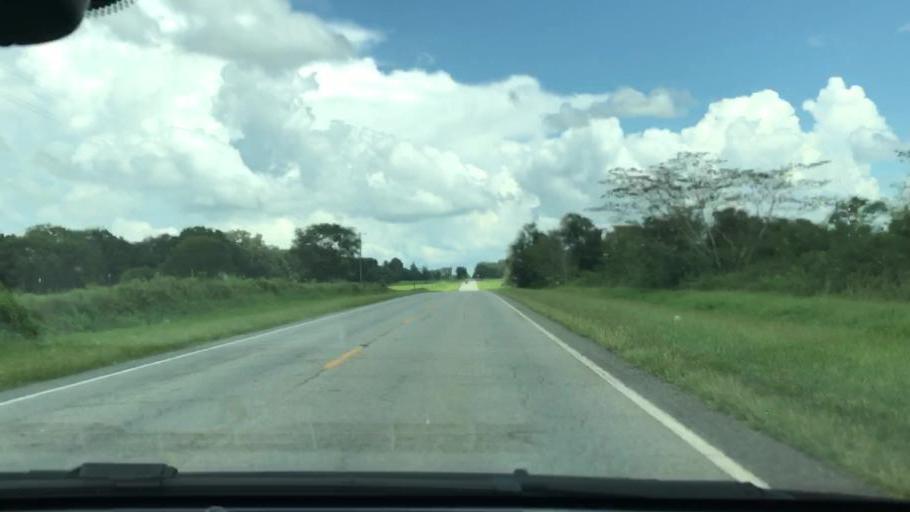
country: US
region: Georgia
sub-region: Seminole County
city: Donalsonville
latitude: 30.9800
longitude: -84.9897
